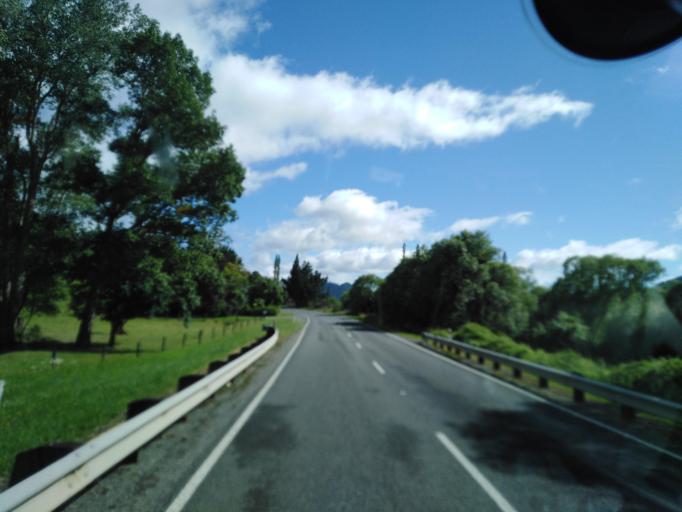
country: NZ
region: Nelson
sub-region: Nelson City
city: Nelson
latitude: -41.2495
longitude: 173.5777
